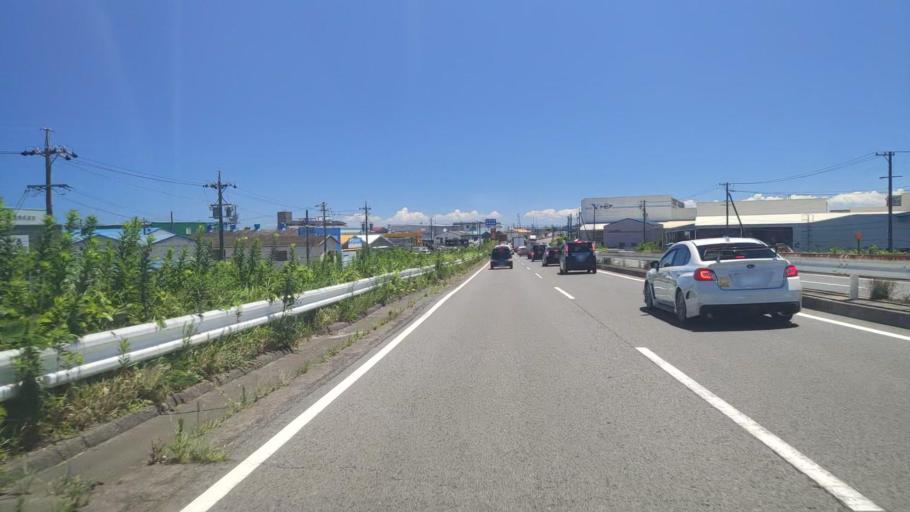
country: JP
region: Mie
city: Suzuka
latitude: 34.9054
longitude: 136.6057
